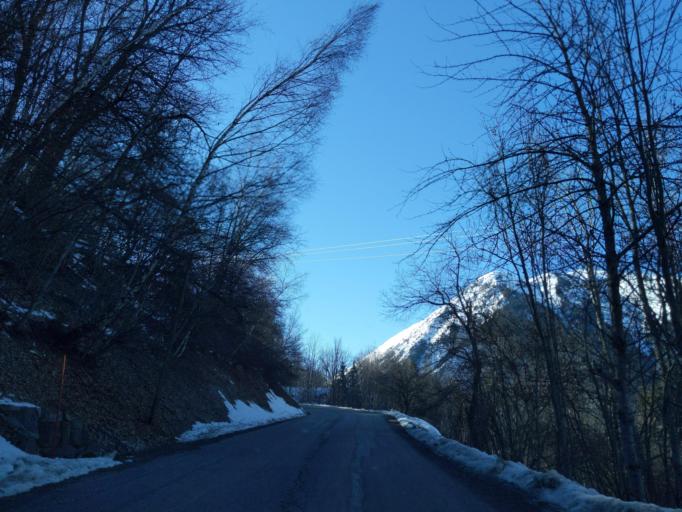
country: FR
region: Rhone-Alpes
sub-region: Departement de la Savoie
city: Saint-Martin-de-Belleville
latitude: 45.4164
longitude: 6.4950
